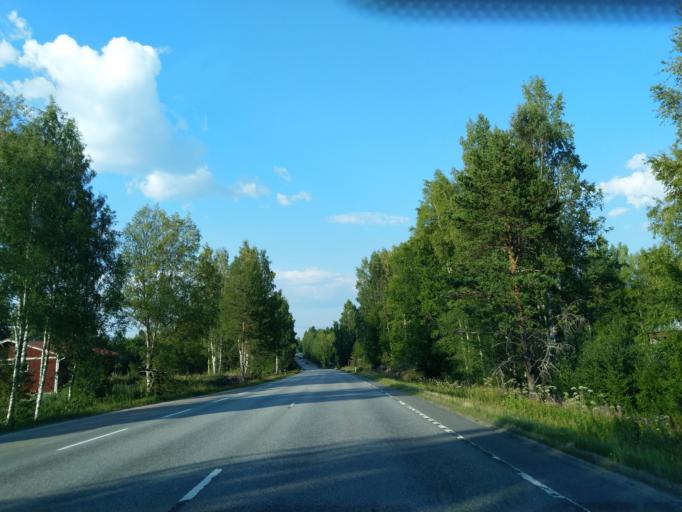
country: FI
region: Satakunta
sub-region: Pori
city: Laengelmaeki
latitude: 61.7555
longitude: 22.1297
